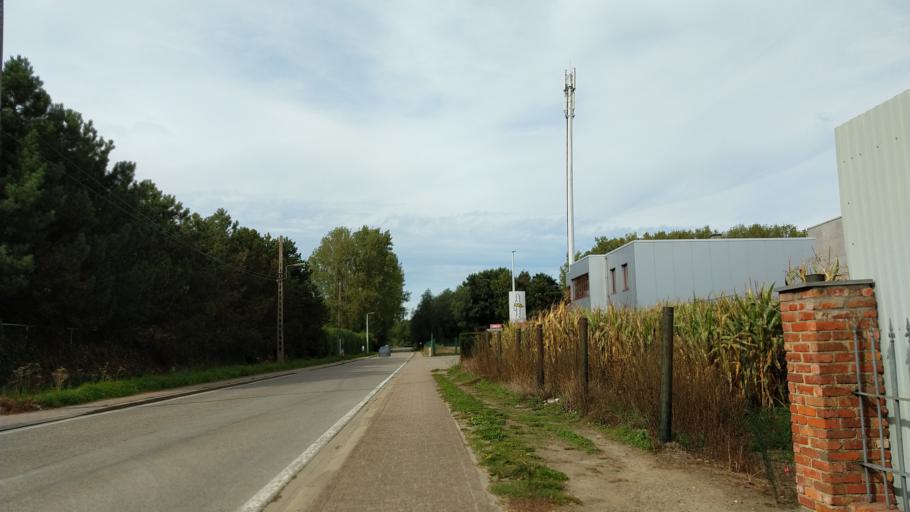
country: BE
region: Flanders
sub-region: Provincie Vlaams-Brabant
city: Tremelo
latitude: 50.9764
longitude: 4.7023
